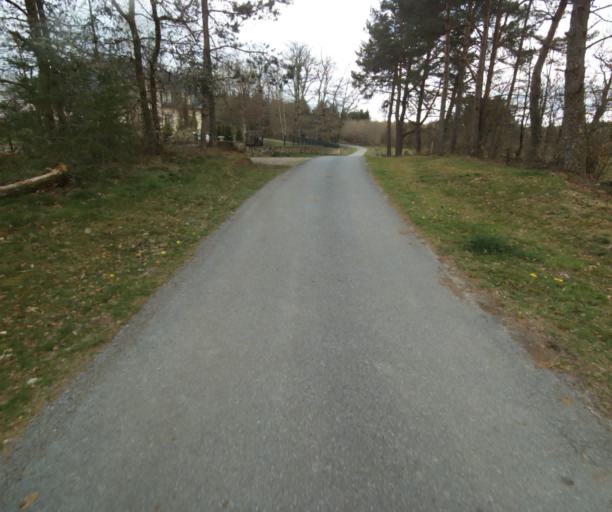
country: FR
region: Limousin
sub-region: Departement de la Correze
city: Correze
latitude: 45.2686
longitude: 1.9554
